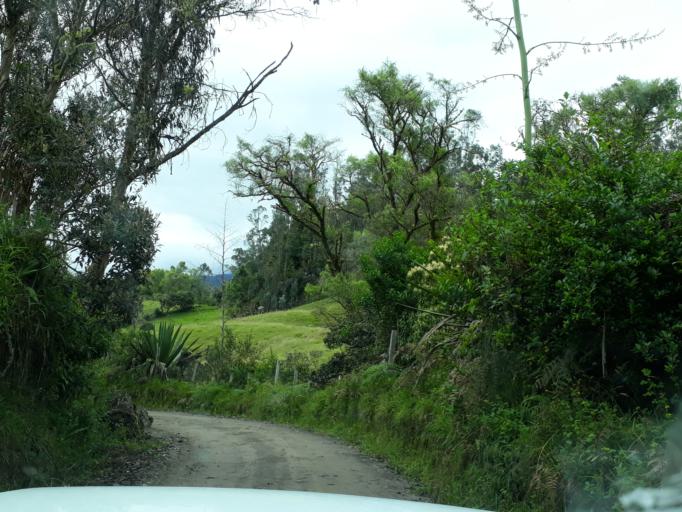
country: CO
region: Cundinamarca
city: Junin
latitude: 4.7974
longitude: -73.6580
